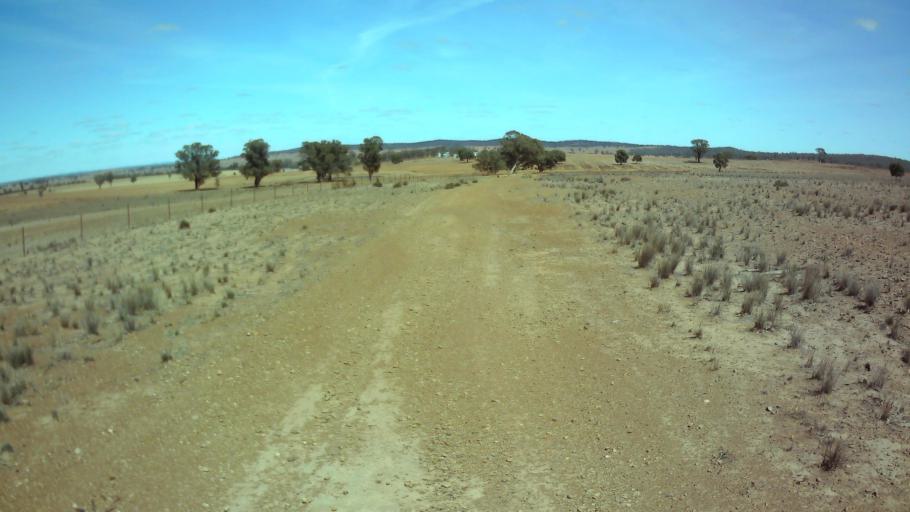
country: AU
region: New South Wales
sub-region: Forbes
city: Forbes
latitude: -33.7184
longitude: 147.8228
